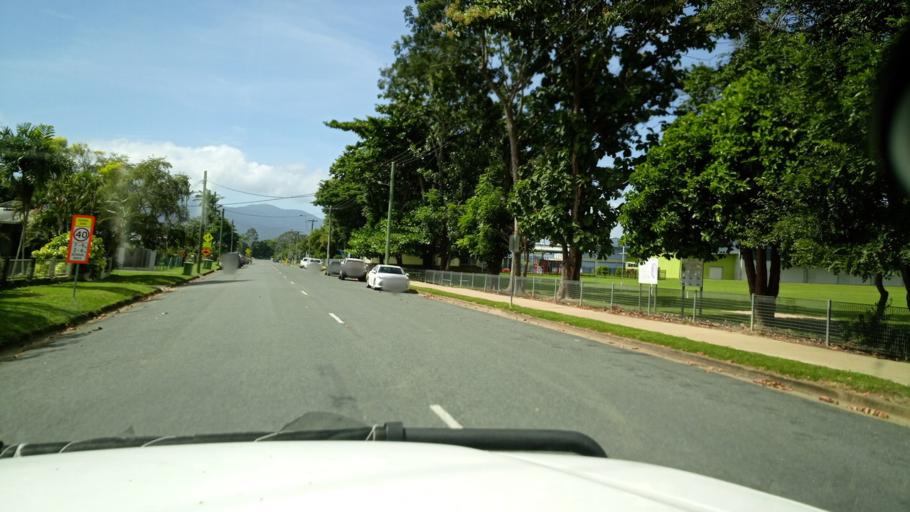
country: AU
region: Queensland
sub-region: Cairns
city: Woree
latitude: -17.0891
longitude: 145.7832
